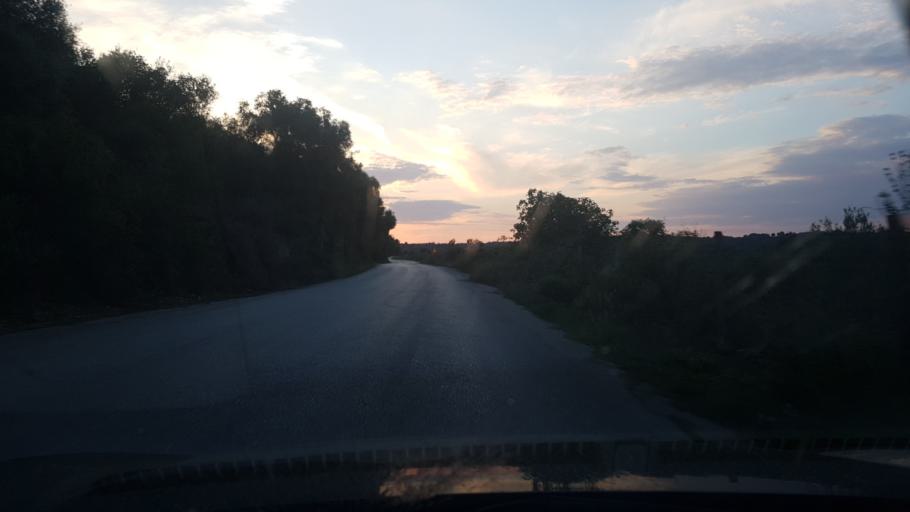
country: GR
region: West Greece
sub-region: Nomos Aitolias kai Akarnanias
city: Vonitsa
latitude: 38.9152
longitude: 20.8746
